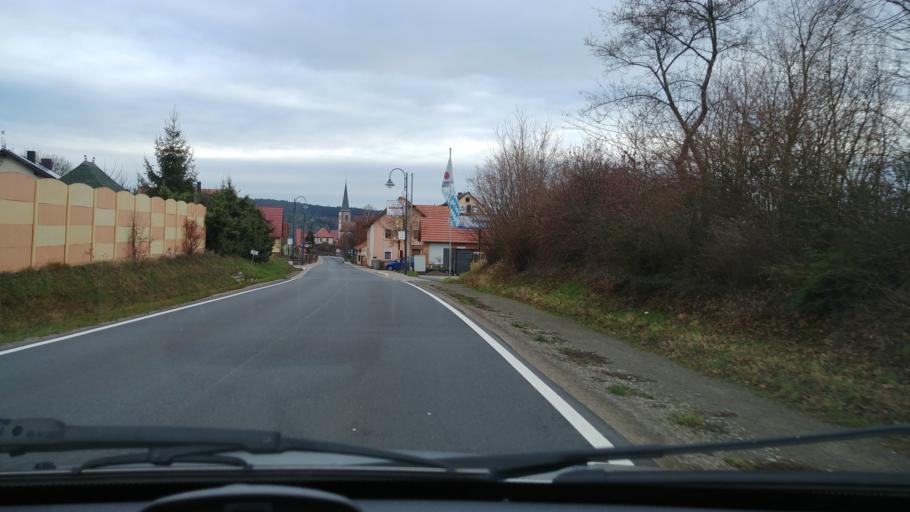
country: DE
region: Bavaria
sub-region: Regierungsbezirk Unterfranken
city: Erlenbach
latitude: 49.9933
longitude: 9.6745
